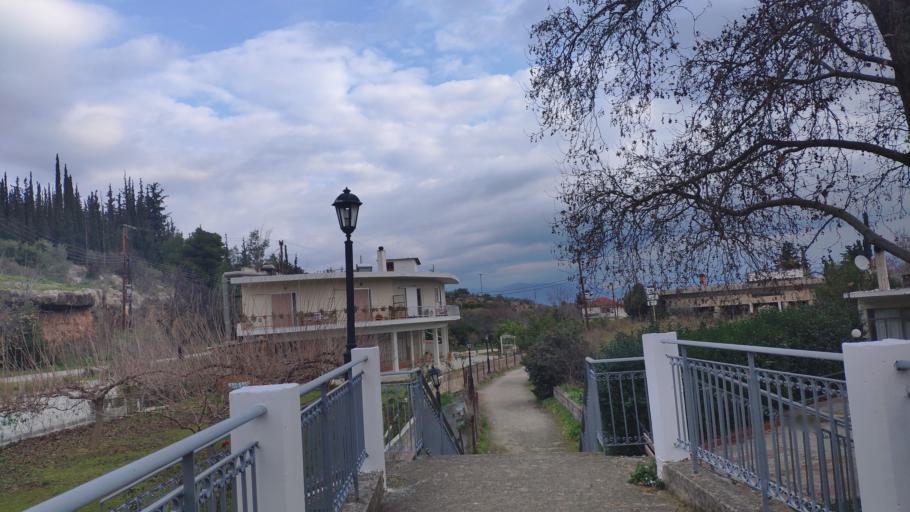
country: GR
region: Peloponnese
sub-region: Nomos Argolidos
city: Nea Kios
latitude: 37.5961
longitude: 22.6882
